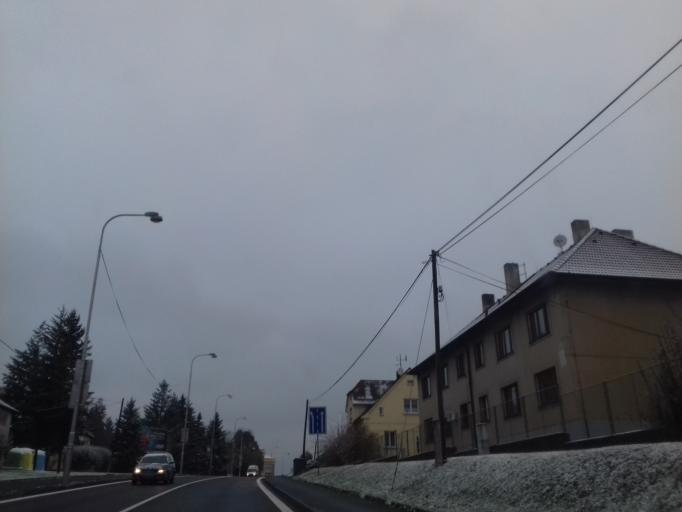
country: CZ
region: Plzensky
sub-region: Okres Domazlice
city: Domazlice
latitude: 49.4411
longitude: 12.9191
